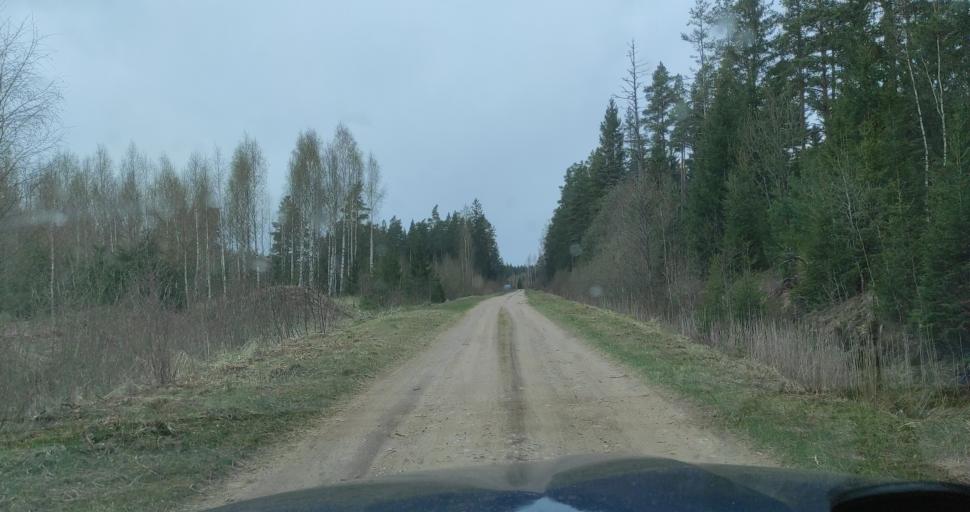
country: LV
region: Dundaga
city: Dundaga
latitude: 57.3580
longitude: 22.1529
